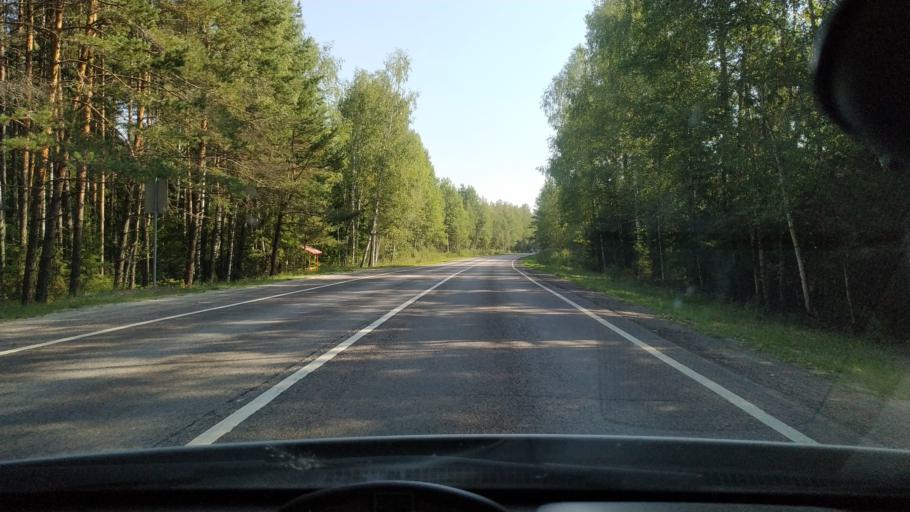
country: RU
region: Moskovskaya
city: Dmitrovskiy Pogost
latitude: 55.2319
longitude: 39.9482
